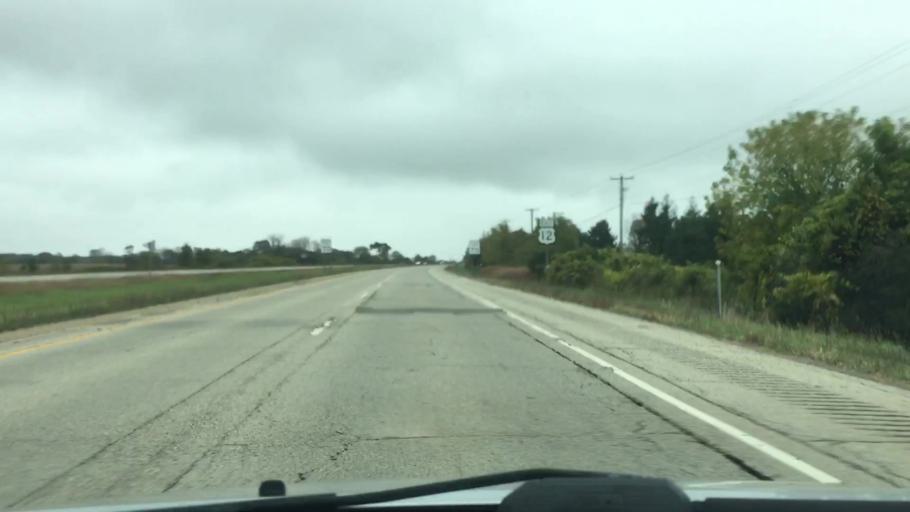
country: US
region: Wisconsin
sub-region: Walworth County
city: Elkhorn
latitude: 42.6919
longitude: -88.5355
